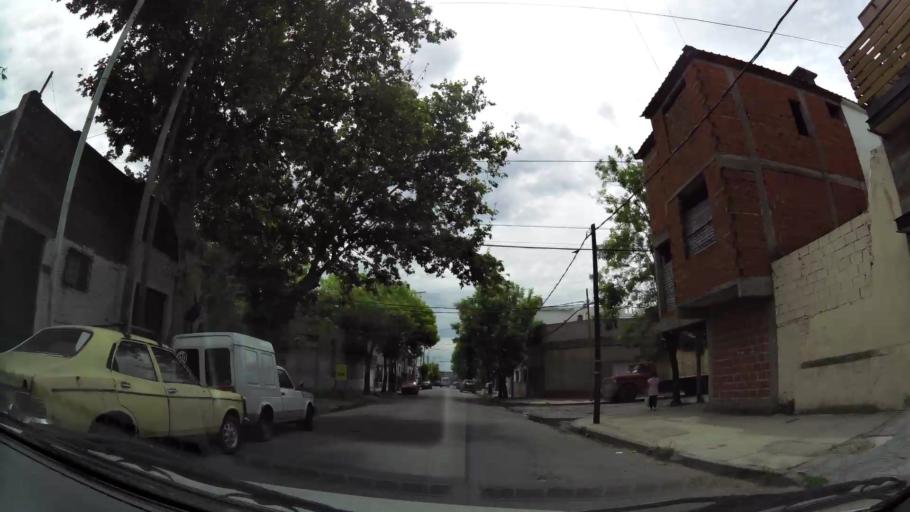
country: AR
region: Buenos Aires
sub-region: Partido de Lanus
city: Lanus
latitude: -34.6693
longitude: -58.4154
